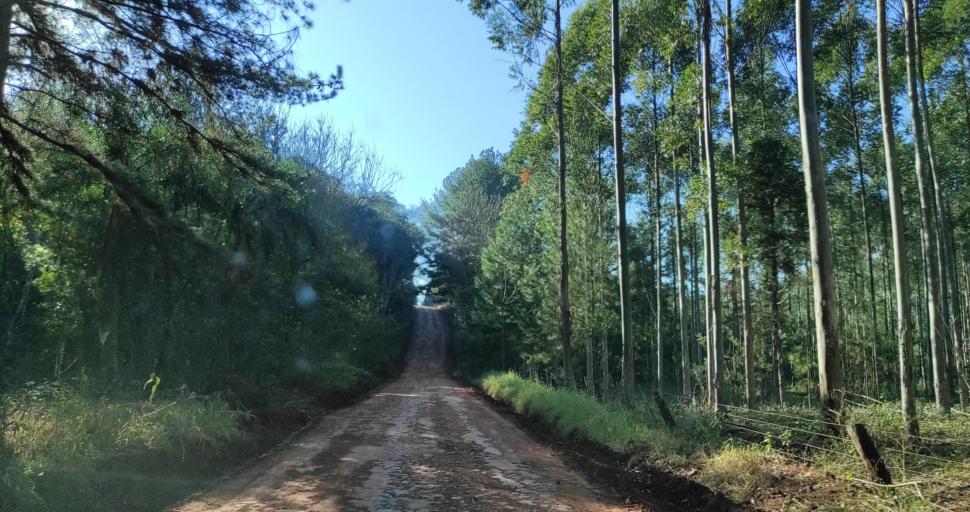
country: AR
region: Misiones
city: Capiovi
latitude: -26.8801
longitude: -55.0279
